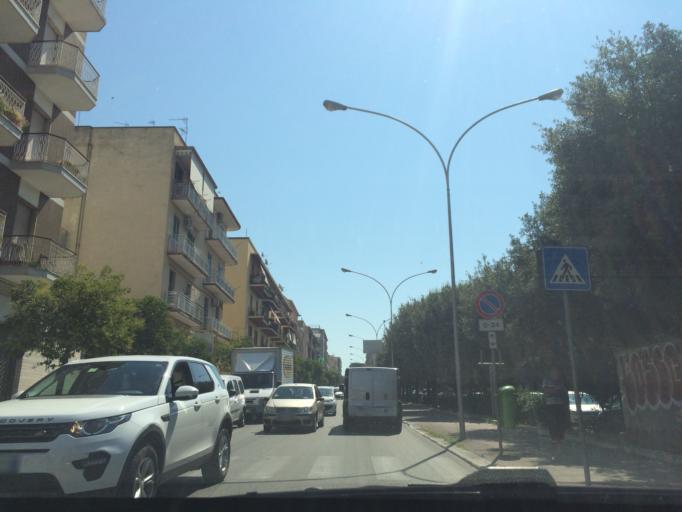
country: IT
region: Basilicate
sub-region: Provincia di Matera
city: Matera
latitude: 40.6751
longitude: 16.5967
